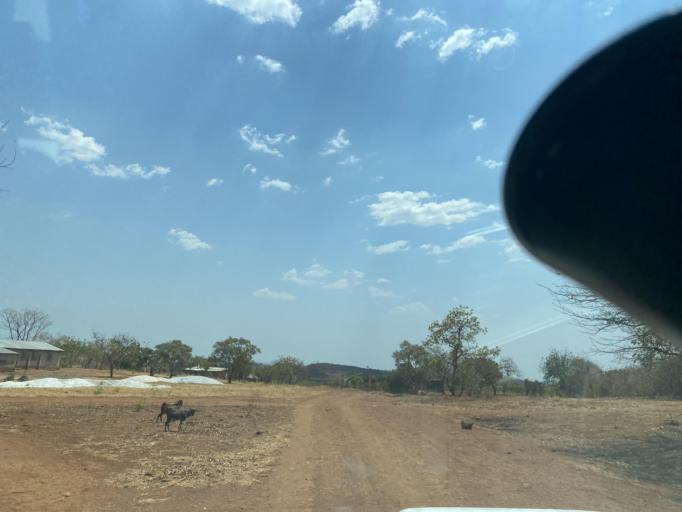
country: ZM
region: Lusaka
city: Lusaka
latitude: -15.4984
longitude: 27.9517
